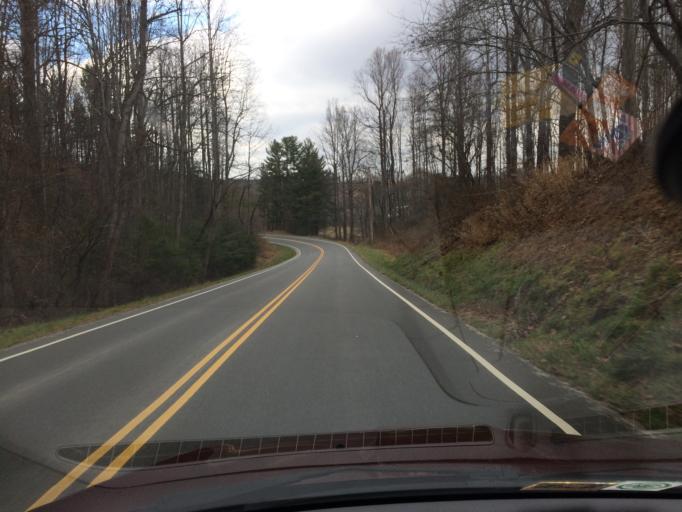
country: US
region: Virginia
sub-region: Patrick County
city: Stuart
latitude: 36.7415
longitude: -80.2509
